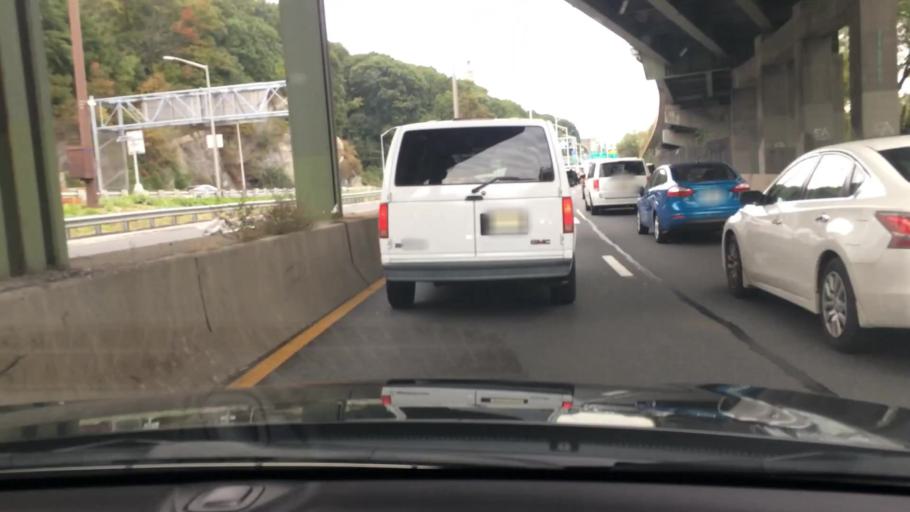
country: US
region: New York
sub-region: New York County
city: Inwood
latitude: 40.8357
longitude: -73.9350
